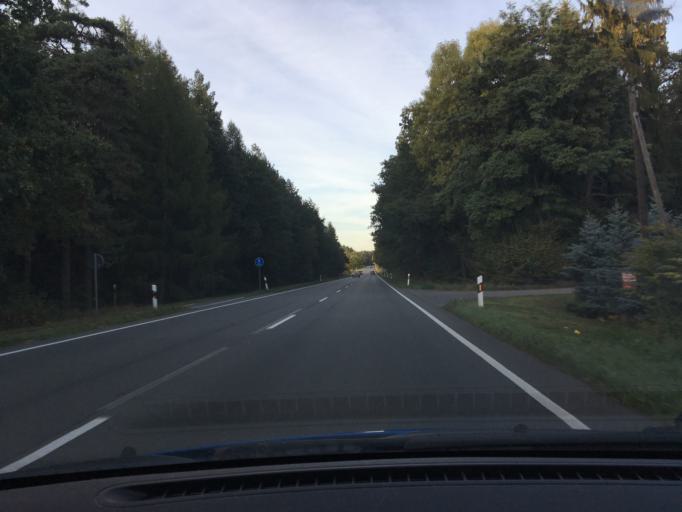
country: DE
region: Lower Saxony
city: Betzendorf
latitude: 53.1636
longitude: 10.3031
